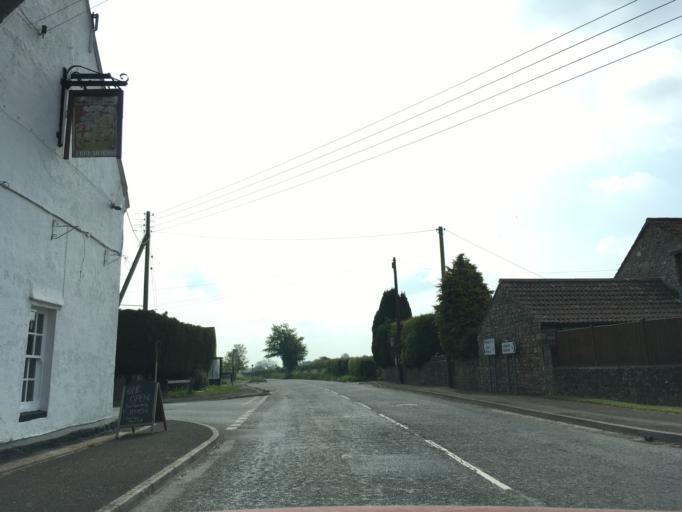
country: GB
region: England
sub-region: North Somerset
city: Winford
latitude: 51.3867
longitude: -2.6892
